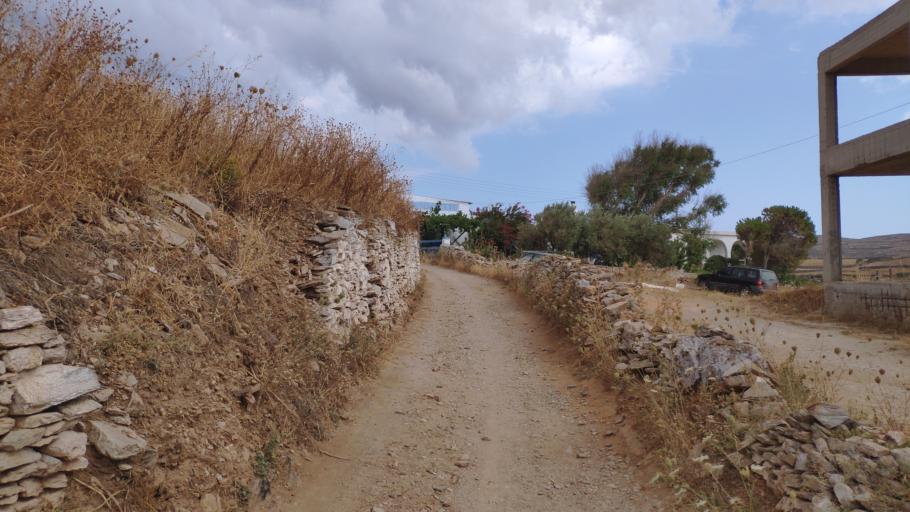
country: GR
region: South Aegean
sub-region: Nomos Kykladon
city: Kythnos
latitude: 37.4122
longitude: 24.4261
